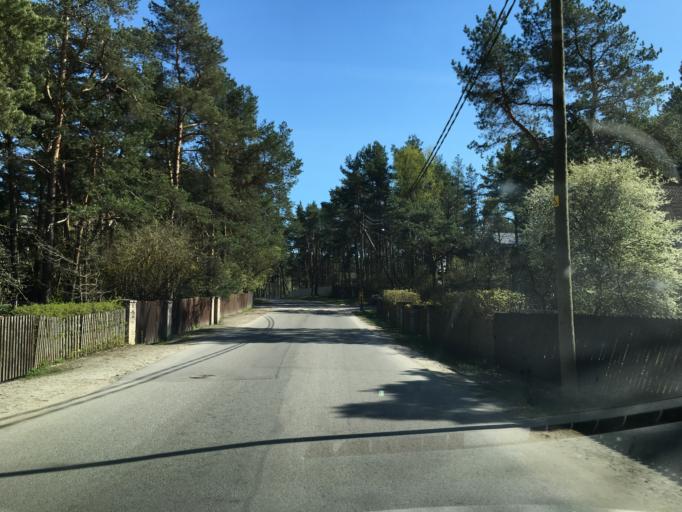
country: EE
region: Harju
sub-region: Tallinna linn
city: Tallinn
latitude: 59.3891
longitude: 24.7102
